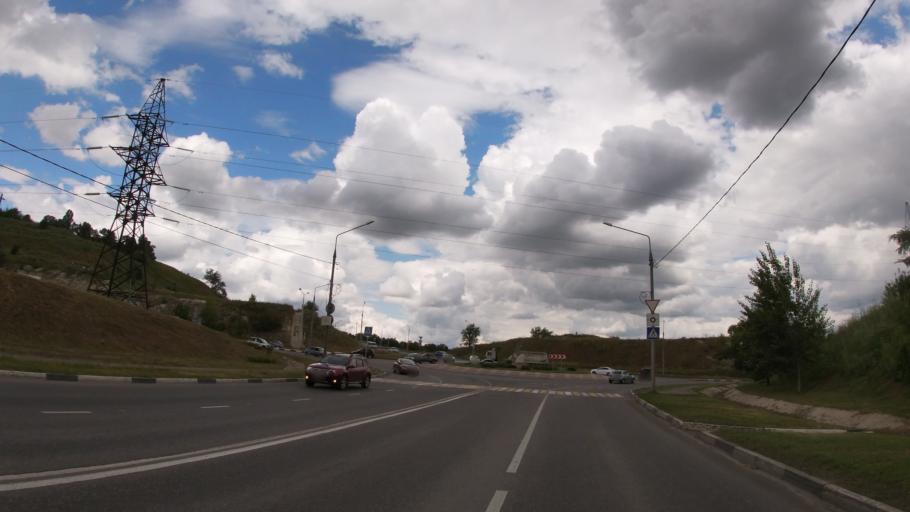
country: RU
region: Belgorod
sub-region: Belgorodskiy Rayon
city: Belgorod
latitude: 50.6169
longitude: 36.6158
